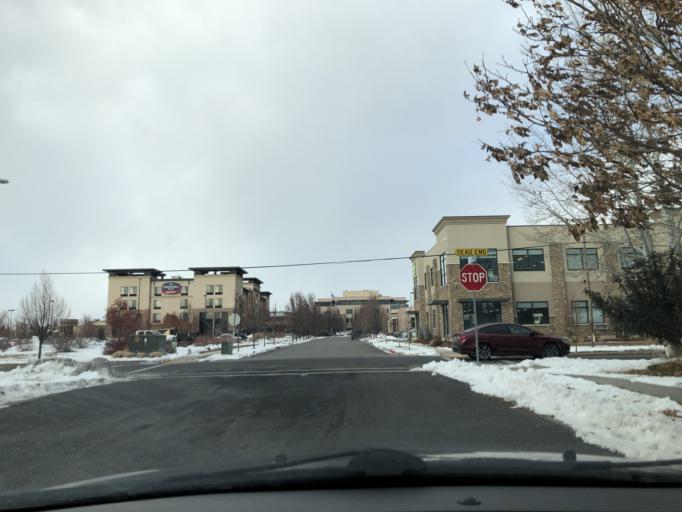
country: US
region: Utah
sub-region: Cache County
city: River Heights
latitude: 41.7190
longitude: -111.8334
